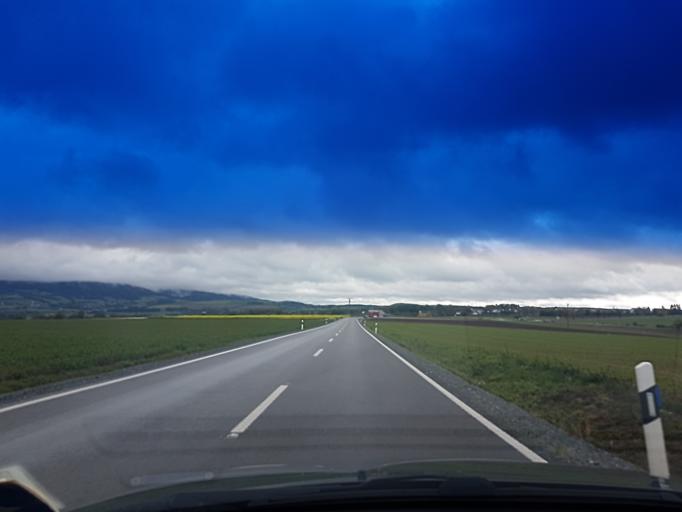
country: DE
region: Bavaria
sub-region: Upper Franconia
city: Bindlach
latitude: 50.0066
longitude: 11.6195
